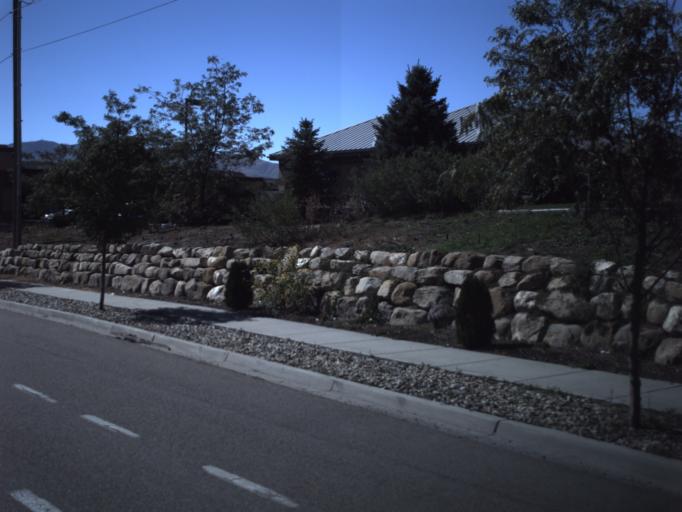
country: US
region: Utah
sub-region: Utah County
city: Saratoga Springs
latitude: 40.3987
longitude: -111.9191
